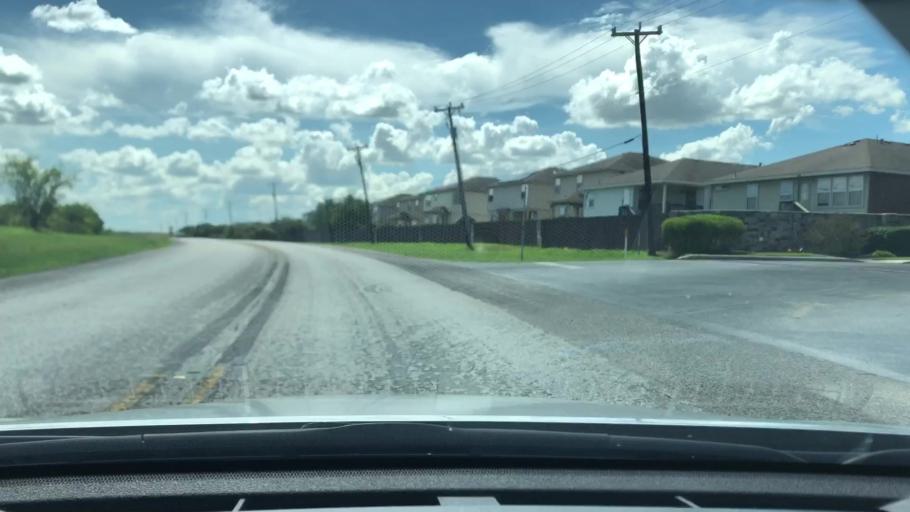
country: US
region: Texas
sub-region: Bexar County
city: Converse
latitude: 29.5315
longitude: -98.3057
